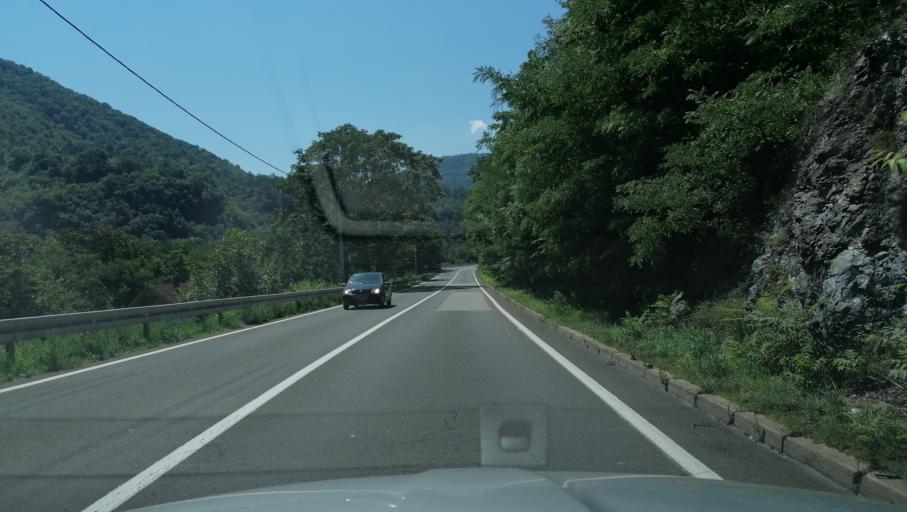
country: RS
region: Central Serbia
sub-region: Raski Okrug
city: Kraljevo
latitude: 43.6372
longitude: 20.5502
